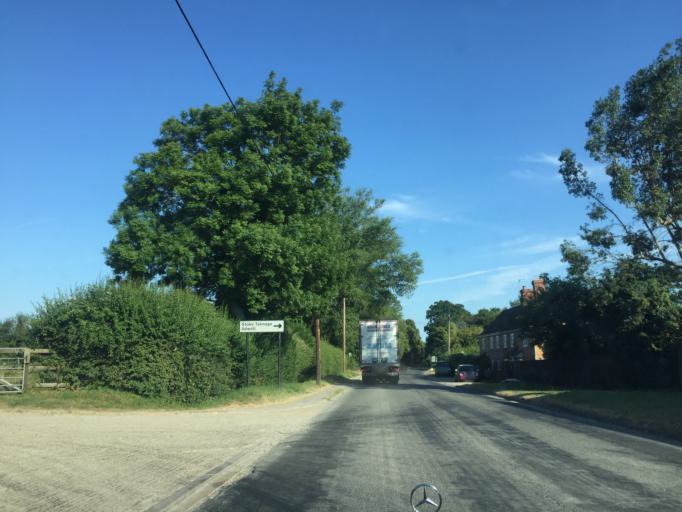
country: GB
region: England
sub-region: Oxfordshire
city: Thame
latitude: 51.7069
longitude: -1.0022
